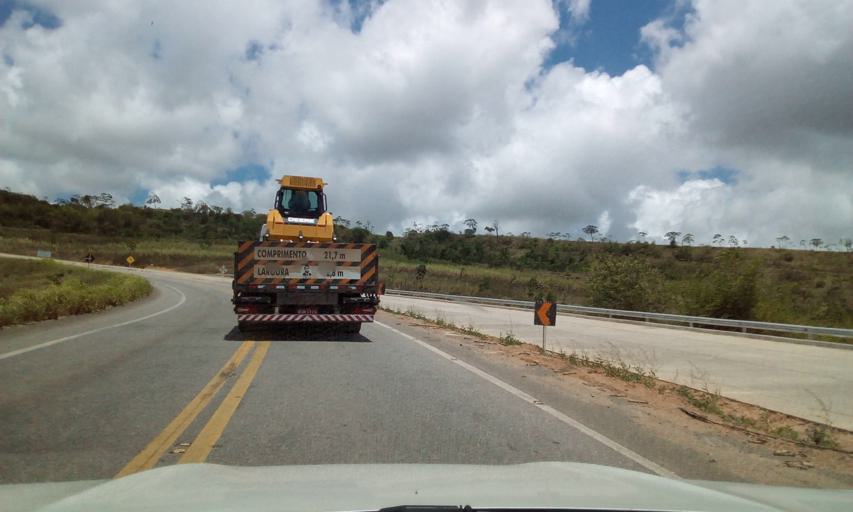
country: BR
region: Alagoas
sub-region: Sao Miguel Dos Campos
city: Sao Miguel dos Campos
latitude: -9.8909
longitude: -36.1353
